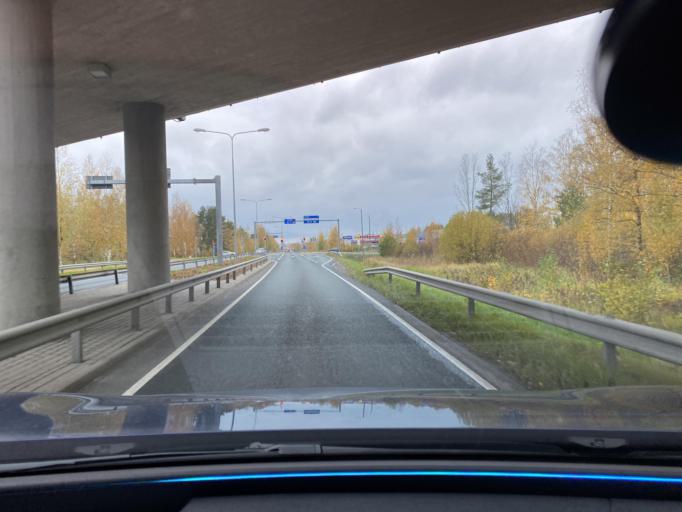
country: FI
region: Satakunta
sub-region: Rauma
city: Rauma
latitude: 61.1326
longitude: 21.5348
